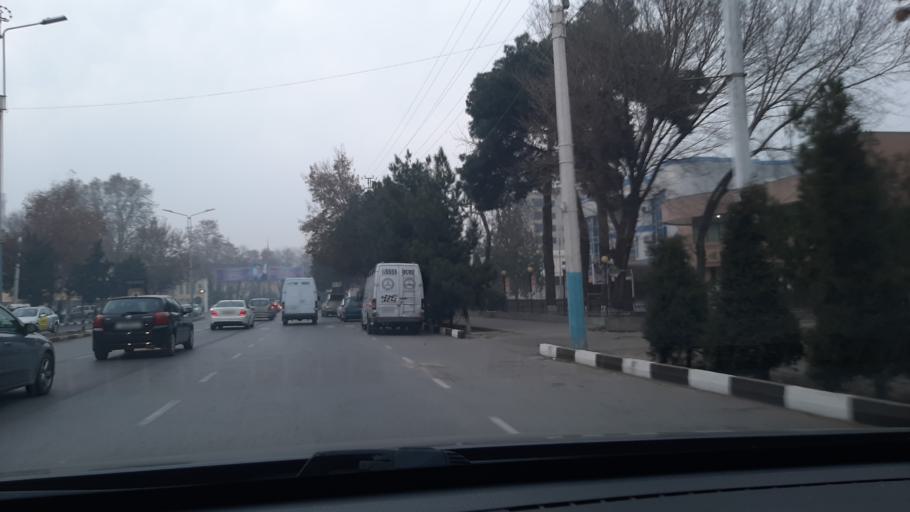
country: TJ
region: Viloyati Sughd
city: Khujand
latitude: 40.2674
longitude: 69.6506
